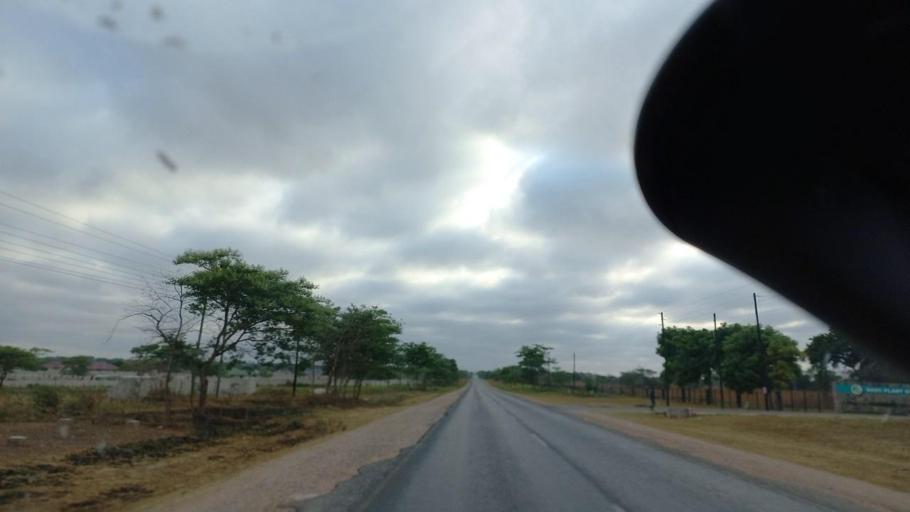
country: ZM
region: Lusaka
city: Chongwe
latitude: -15.3526
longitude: 28.4898
